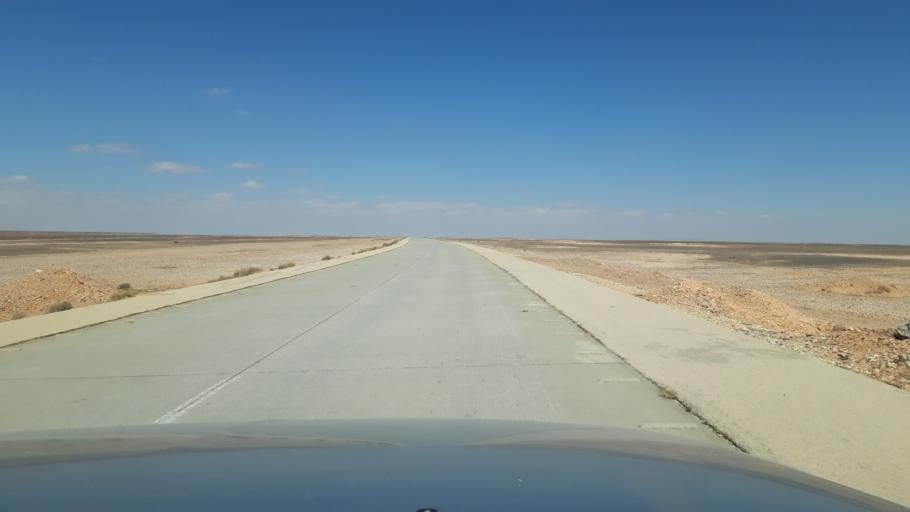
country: JO
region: Amman
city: Al Azraq ash Shamali
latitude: 31.4718
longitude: 36.8061
